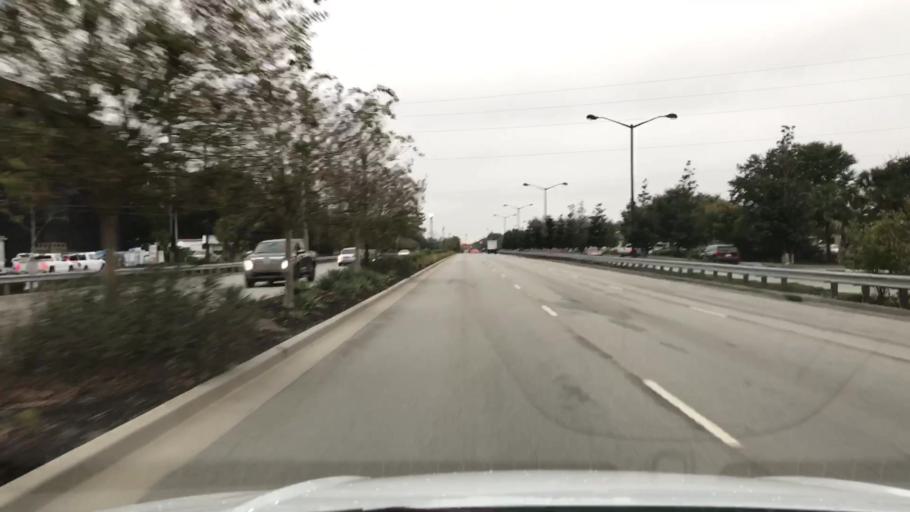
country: US
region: South Carolina
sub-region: Charleston County
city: Mount Pleasant
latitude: 32.8069
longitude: -79.8837
